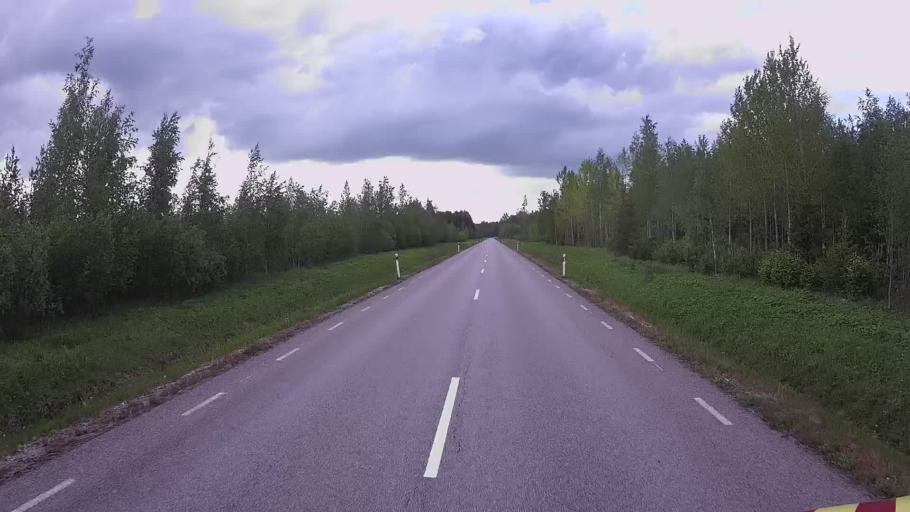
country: EE
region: Jogevamaa
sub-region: Mustvee linn
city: Mustvee
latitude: 59.0831
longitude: 26.9905
